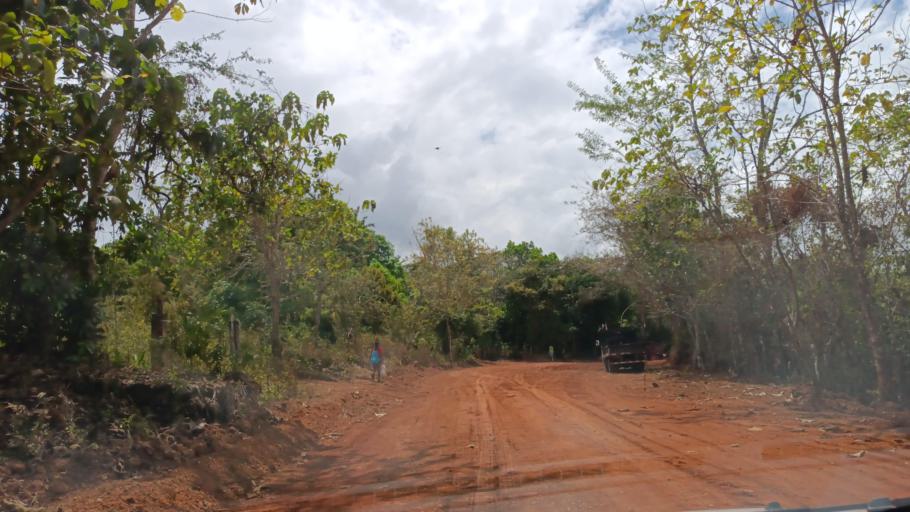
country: PA
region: Panama
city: La Cabima
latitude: 9.1208
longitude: -79.4951
